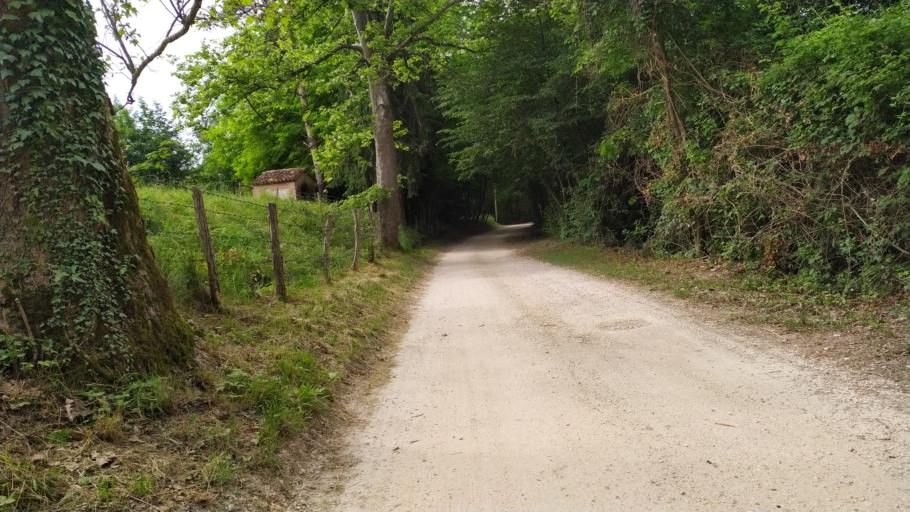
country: IT
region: Veneto
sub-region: Provincia di Treviso
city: Falze di Piave
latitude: 45.8588
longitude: 12.1995
